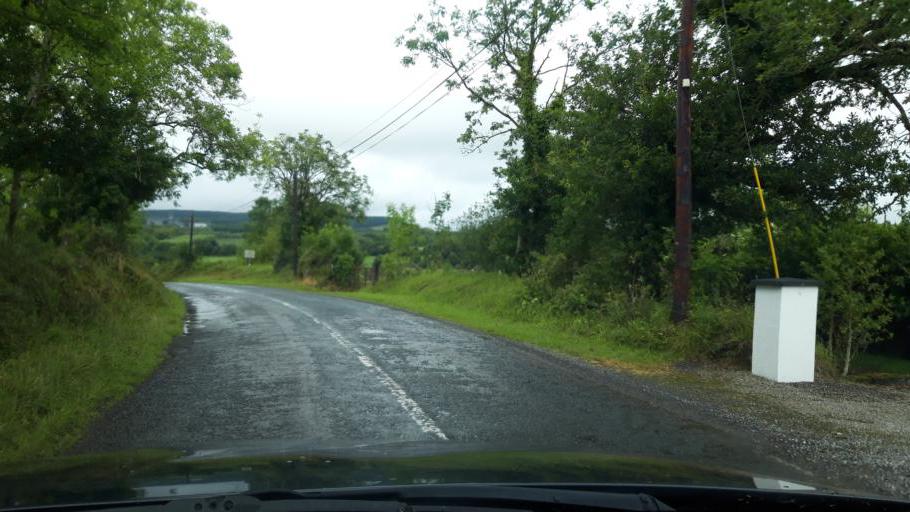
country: IE
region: Munster
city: Cahir
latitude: 52.1696
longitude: -7.8524
